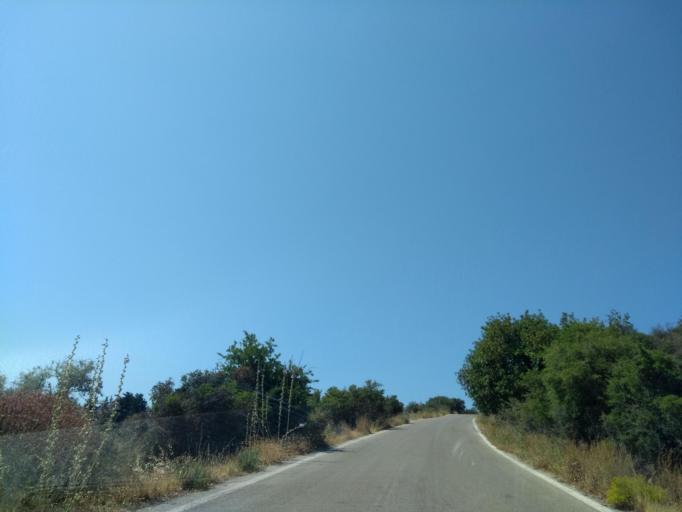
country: GR
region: Crete
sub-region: Nomos Chanias
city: Georgioupolis
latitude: 35.3900
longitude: 24.2357
